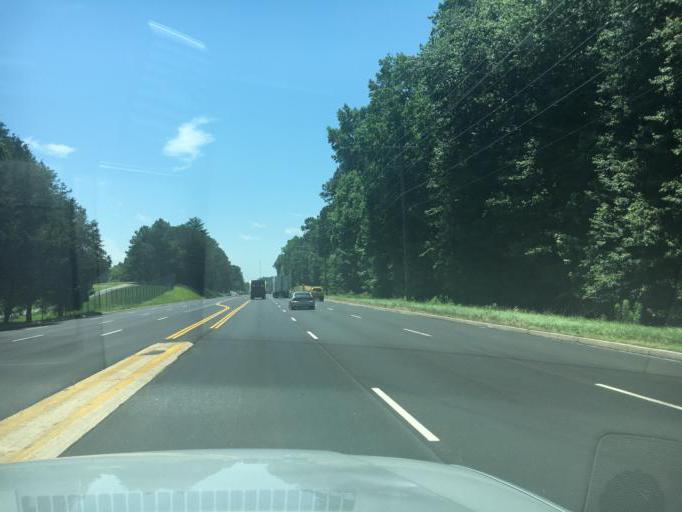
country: US
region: South Carolina
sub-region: Greenville County
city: Travelers Rest
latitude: 34.9321
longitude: -82.4504
